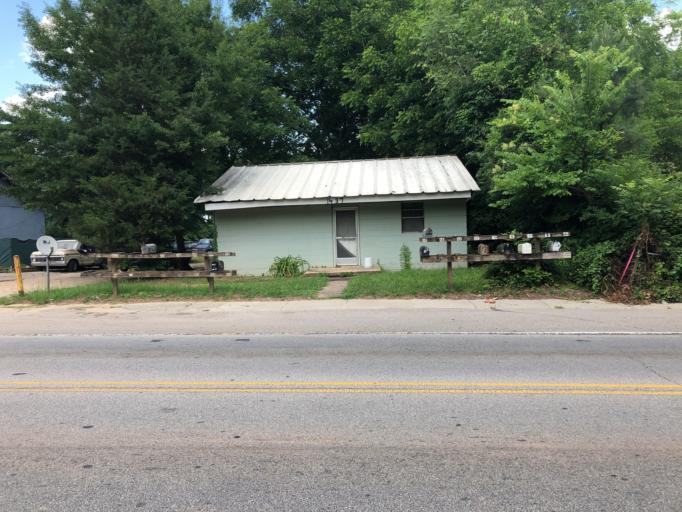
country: US
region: Georgia
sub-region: Troup County
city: La Grange
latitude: 33.0175
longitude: -85.0223
